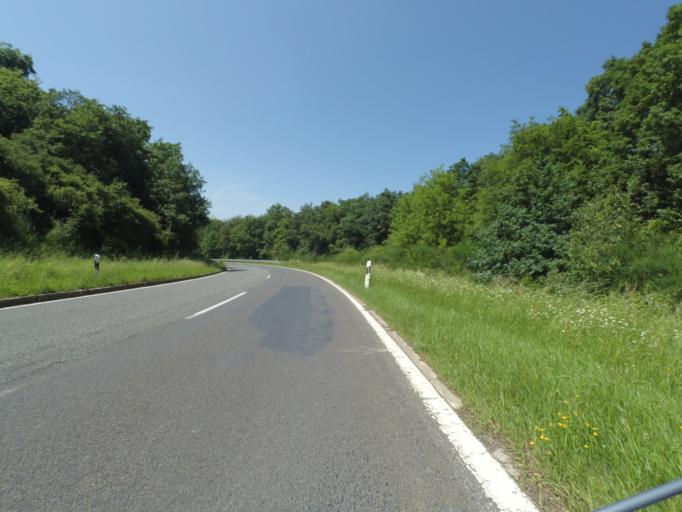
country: DE
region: Rheinland-Pfalz
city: Altstrimmig
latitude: 50.1211
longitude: 7.3156
